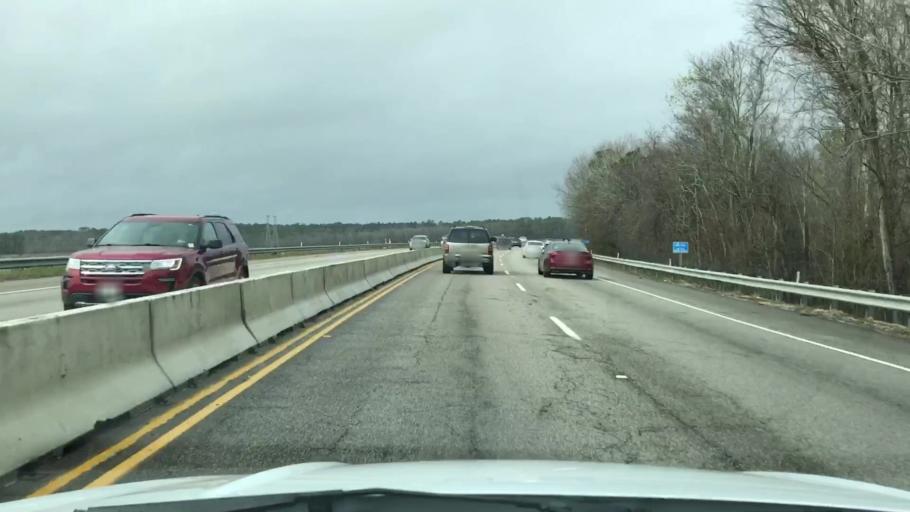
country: US
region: South Carolina
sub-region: Horry County
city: Conway
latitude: 33.8211
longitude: -79.0498
